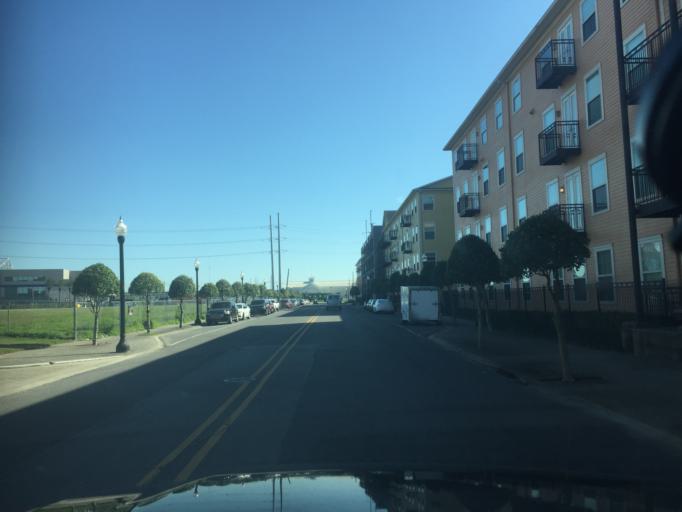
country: US
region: Louisiana
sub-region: Orleans Parish
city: New Orleans
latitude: 29.9345
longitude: -90.0686
